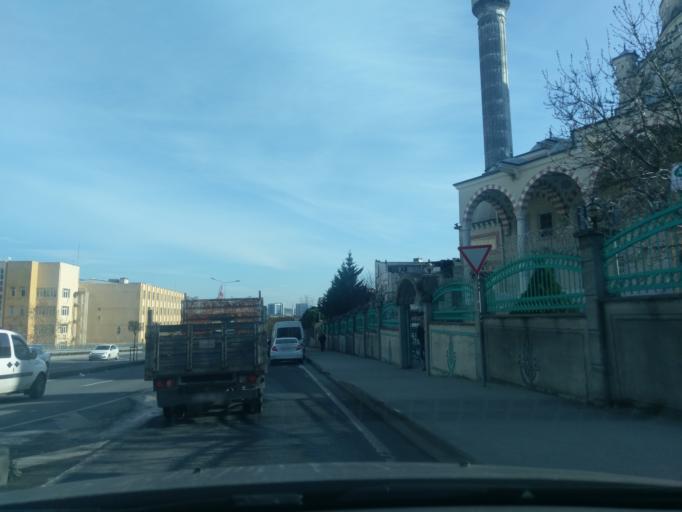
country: TR
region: Istanbul
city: Basaksehir
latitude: 41.0697
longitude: 28.8053
